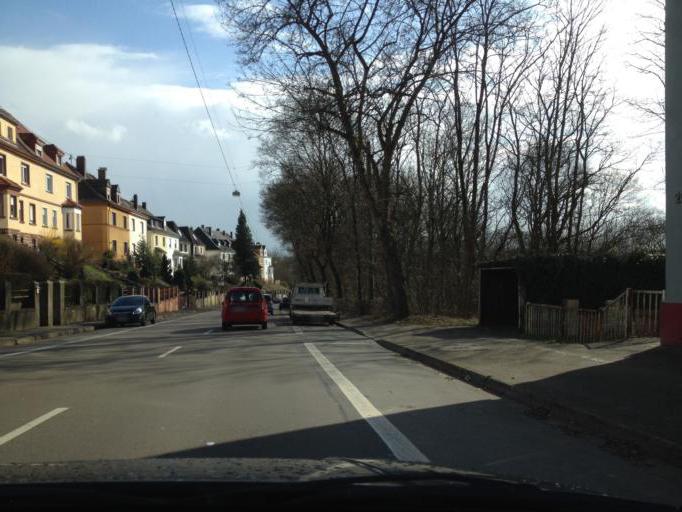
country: DE
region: Saarland
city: Neunkirchen
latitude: 49.3597
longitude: 7.1803
